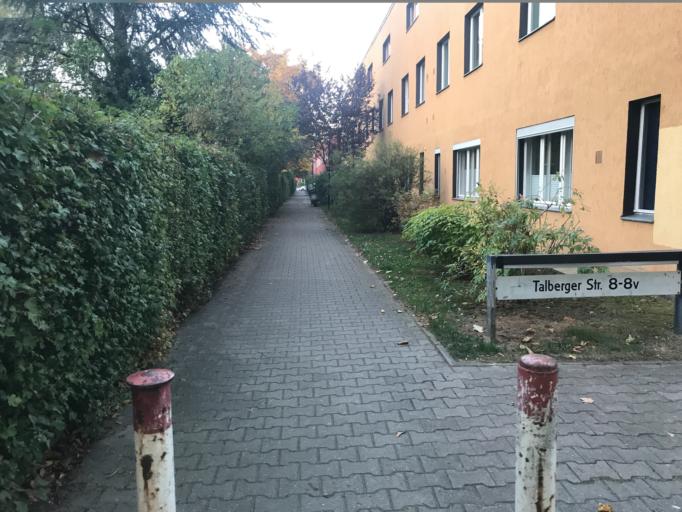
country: DE
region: Berlin
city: Britz
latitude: 52.4432
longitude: 13.4466
